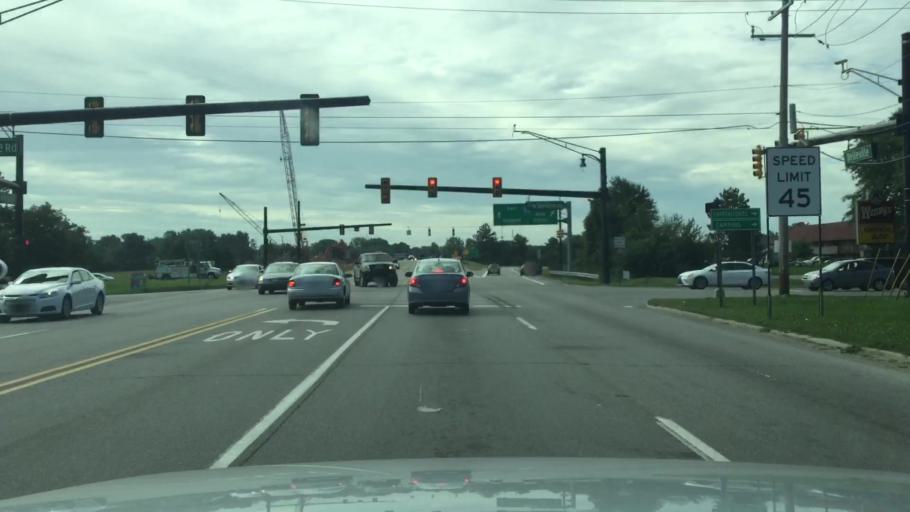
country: US
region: Michigan
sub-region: Wayne County
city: Belleville
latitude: 42.2229
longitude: -83.4852
